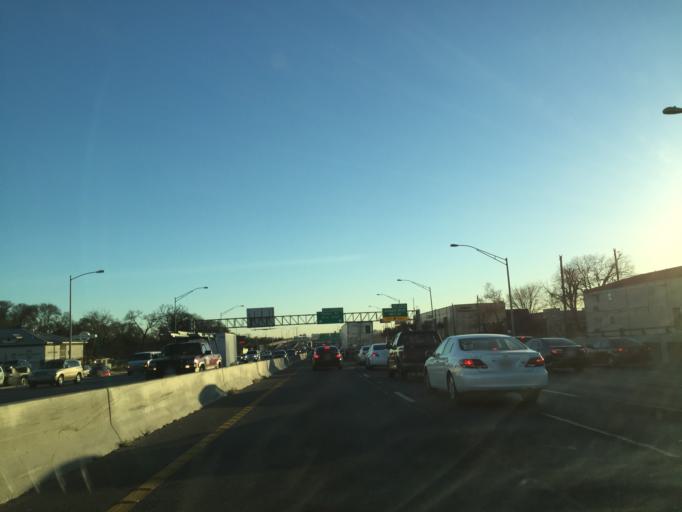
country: US
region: Texas
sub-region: Travis County
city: Austin
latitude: 30.3062
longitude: -97.7125
